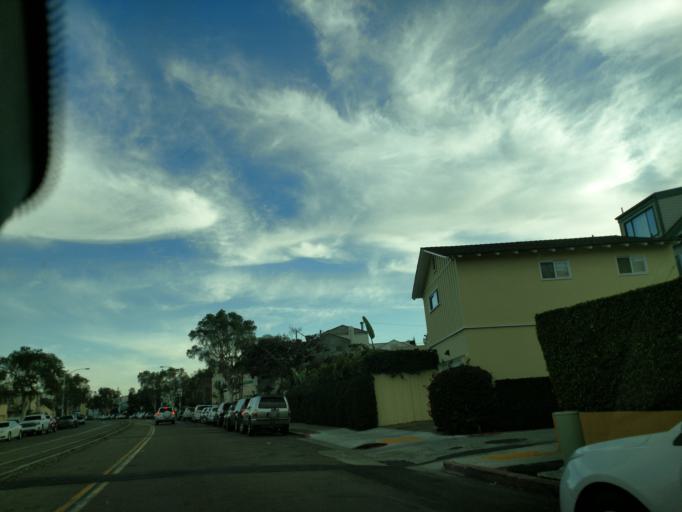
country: US
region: California
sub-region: San Diego County
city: La Jolla
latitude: 32.7624
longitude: -117.2510
